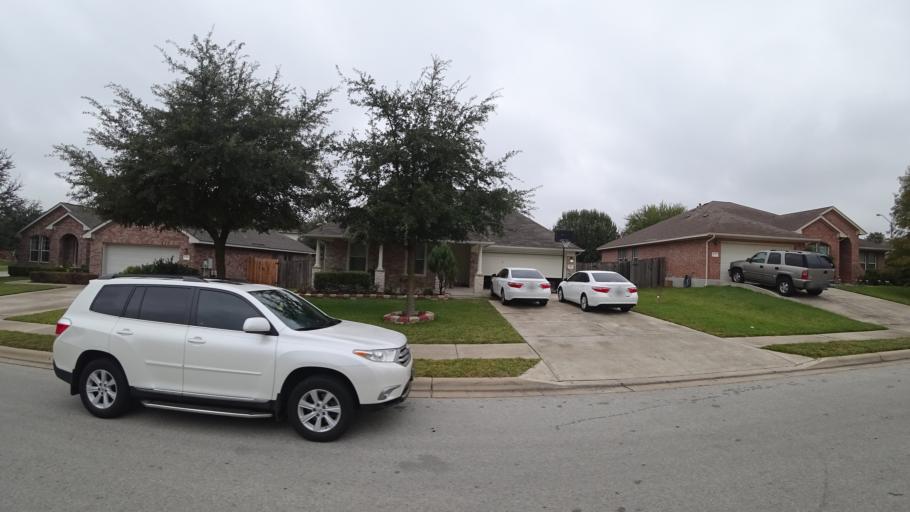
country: US
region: Texas
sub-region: Travis County
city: Pflugerville
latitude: 30.4273
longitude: -97.6186
